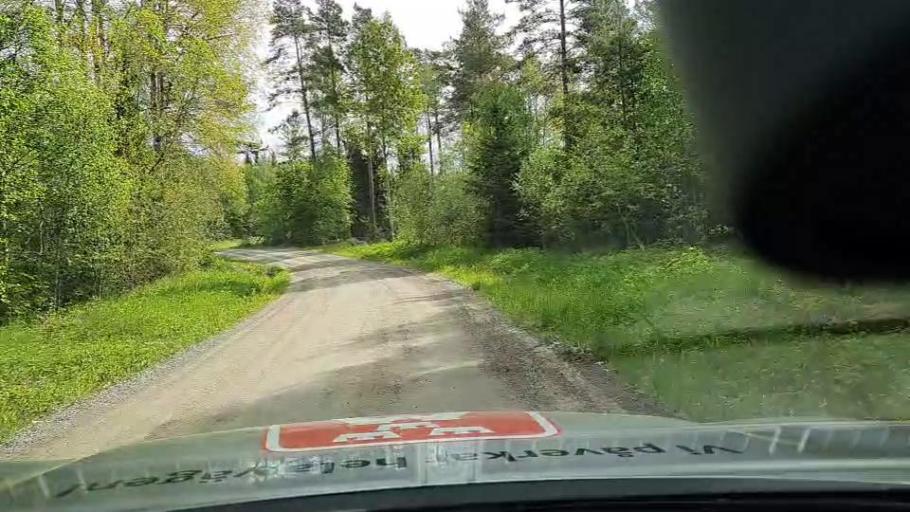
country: SE
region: Soedermanland
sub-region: Eskilstuna Kommun
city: Arla
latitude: 59.2605
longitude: 16.8016
